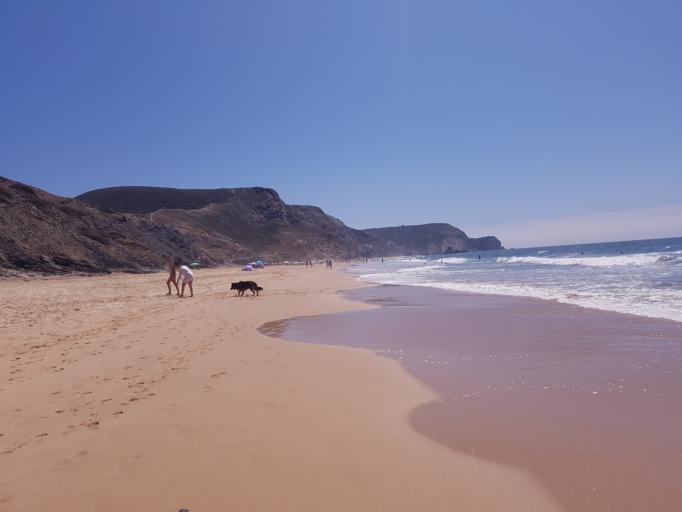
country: PT
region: Faro
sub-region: Vila do Bispo
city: Vila do Bispo
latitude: 37.1120
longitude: -8.9357
